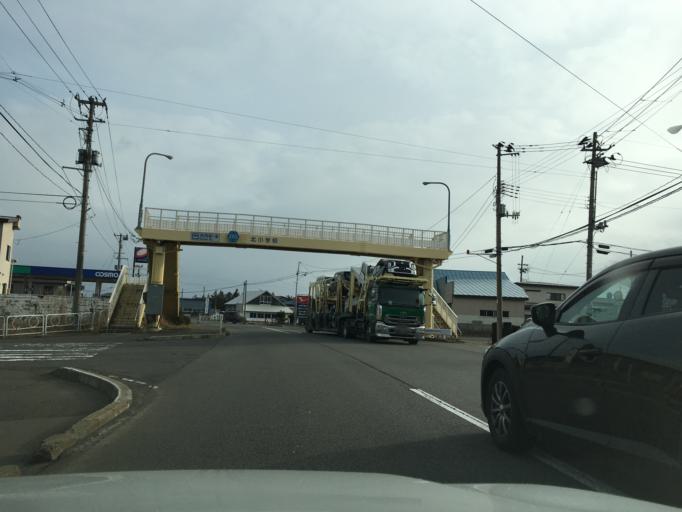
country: JP
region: Aomori
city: Namioka
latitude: 40.7200
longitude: 140.5888
